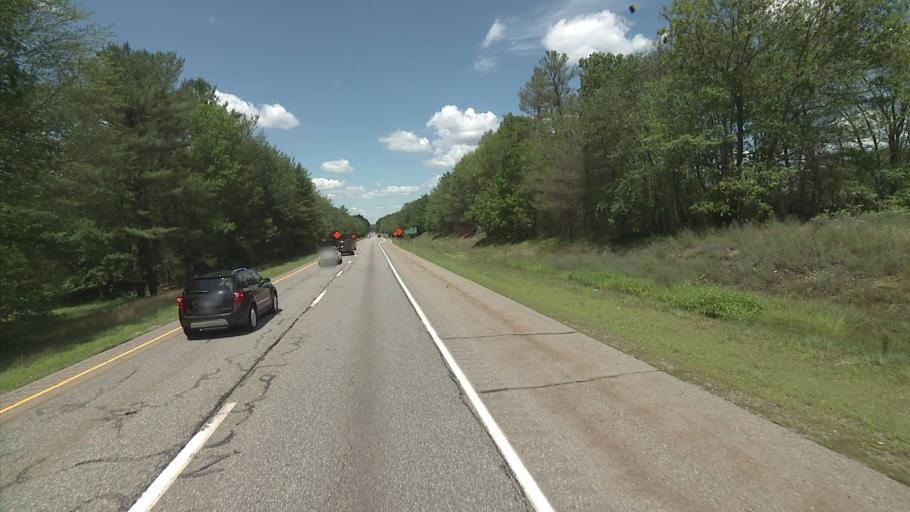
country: US
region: Connecticut
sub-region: Windham County
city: Killingly Center
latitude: 41.8609
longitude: -71.8851
